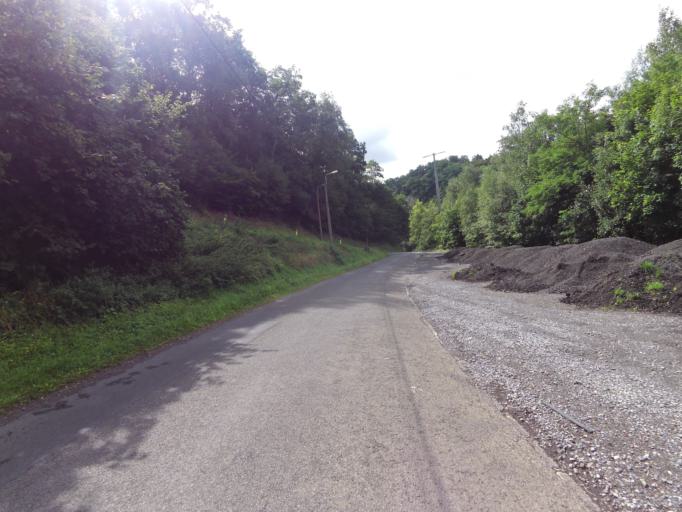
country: BE
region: Wallonia
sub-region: Province de Liege
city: Amay
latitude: 50.5615
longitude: 5.3340
